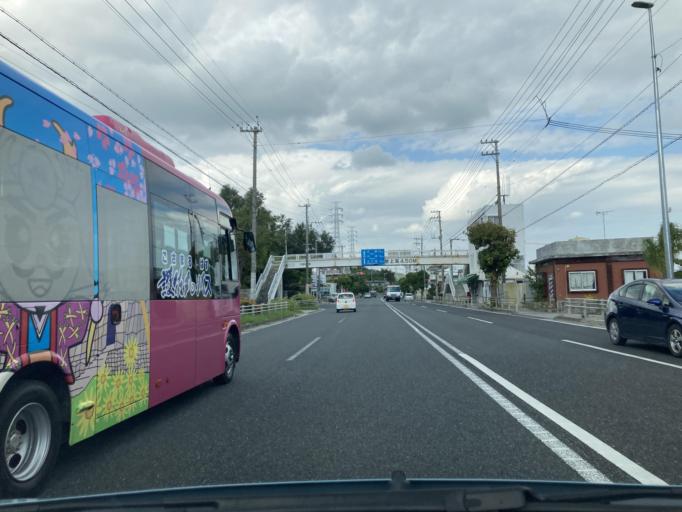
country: JP
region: Okinawa
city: Ginowan
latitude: 26.2479
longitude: 127.7820
